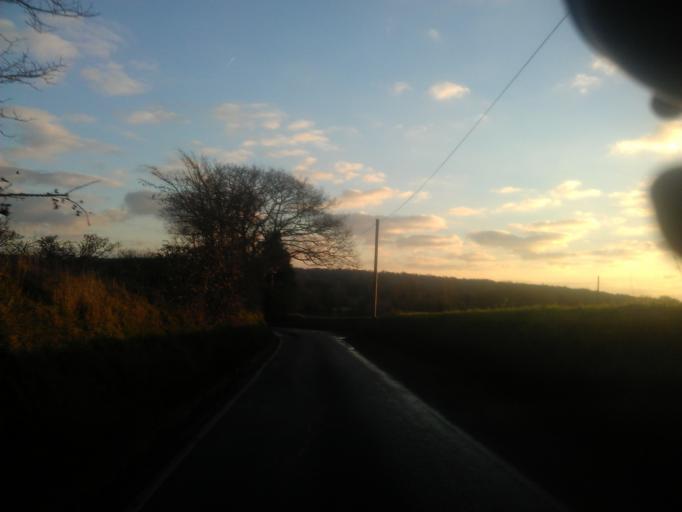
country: GB
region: England
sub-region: Essex
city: Hatfield Peverel
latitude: 51.7555
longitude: 0.5727
